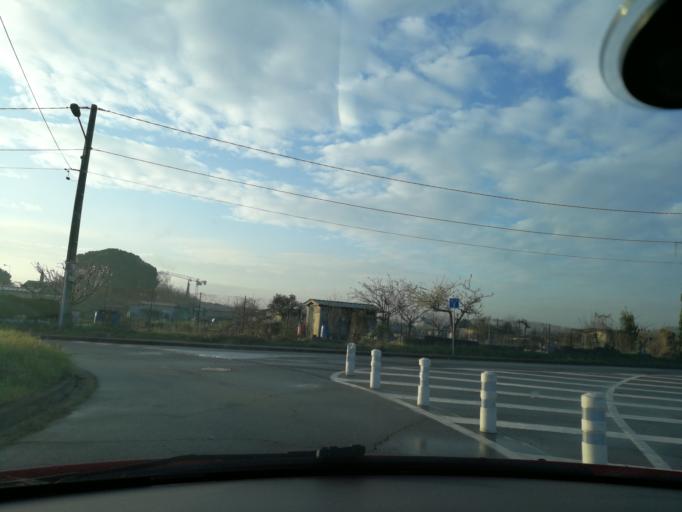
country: FR
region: Midi-Pyrenees
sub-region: Departement de la Haute-Garonne
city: Blagnac
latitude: 43.6382
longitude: 1.4101
